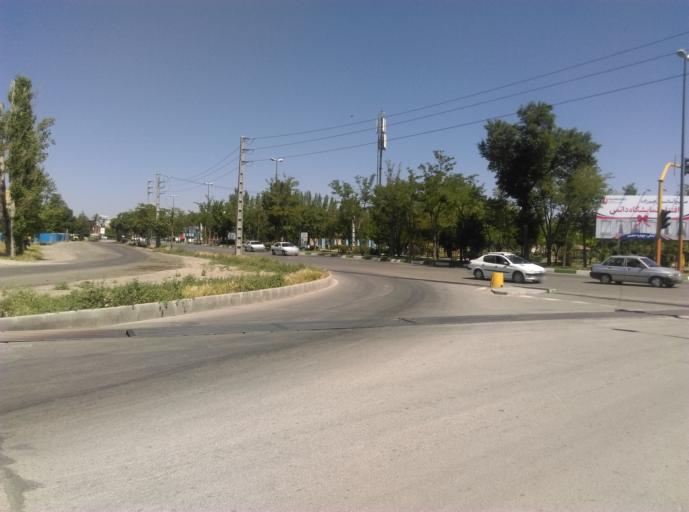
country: IR
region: Ardabil
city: Ardabil
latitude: 38.2246
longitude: 48.2798
